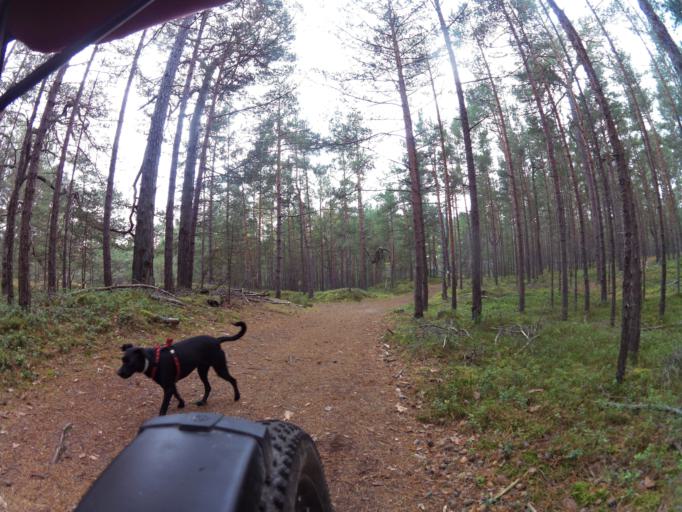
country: PL
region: Pomeranian Voivodeship
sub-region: Powiat pucki
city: Hel
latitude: 54.6240
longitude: 18.8029
